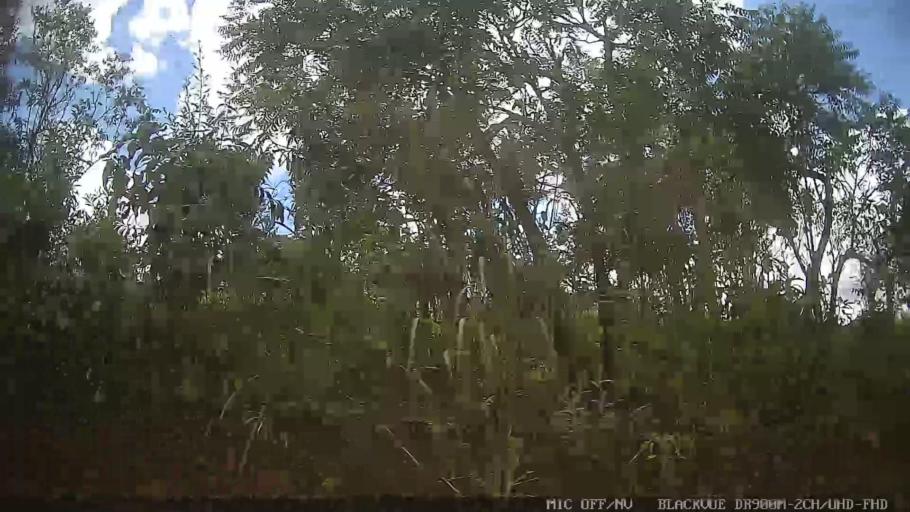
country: BR
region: Sao Paulo
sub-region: Atibaia
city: Atibaia
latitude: -23.1275
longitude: -46.6020
